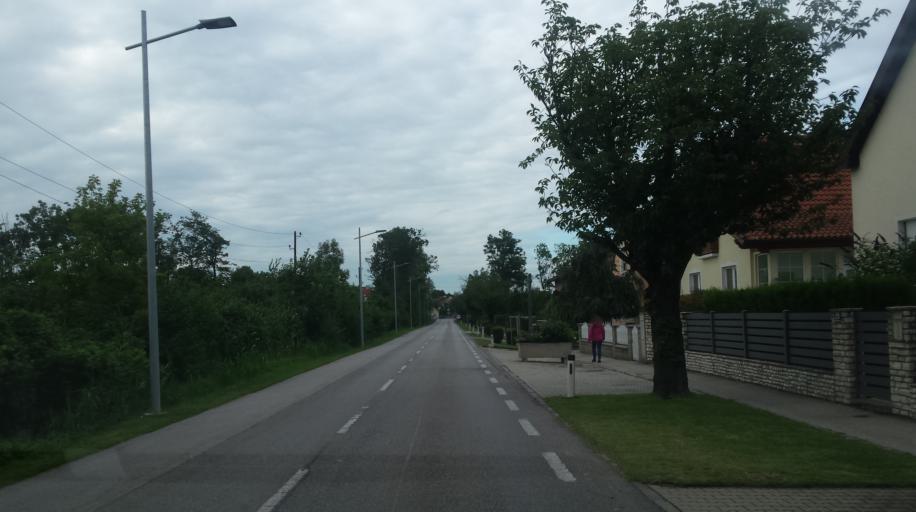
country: AT
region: Lower Austria
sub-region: Politischer Bezirk Wien-Umgebung
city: Moosbrunn
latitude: 48.0139
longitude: 16.4533
